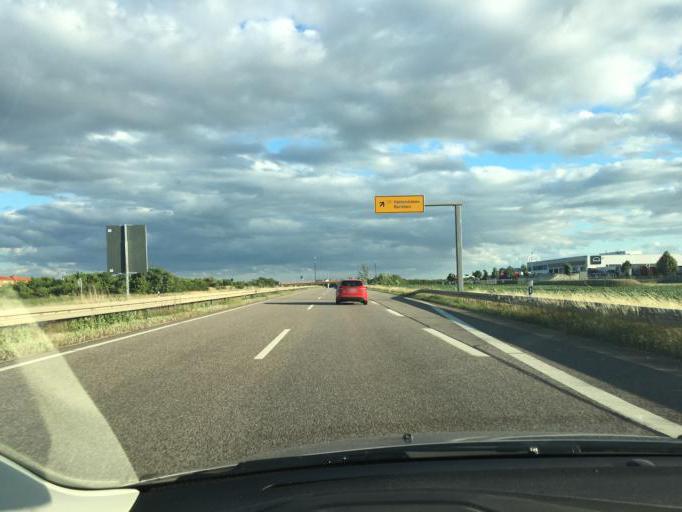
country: DE
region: Saxony-Anhalt
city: Barleben
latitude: 52.2018
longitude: 11.6067
